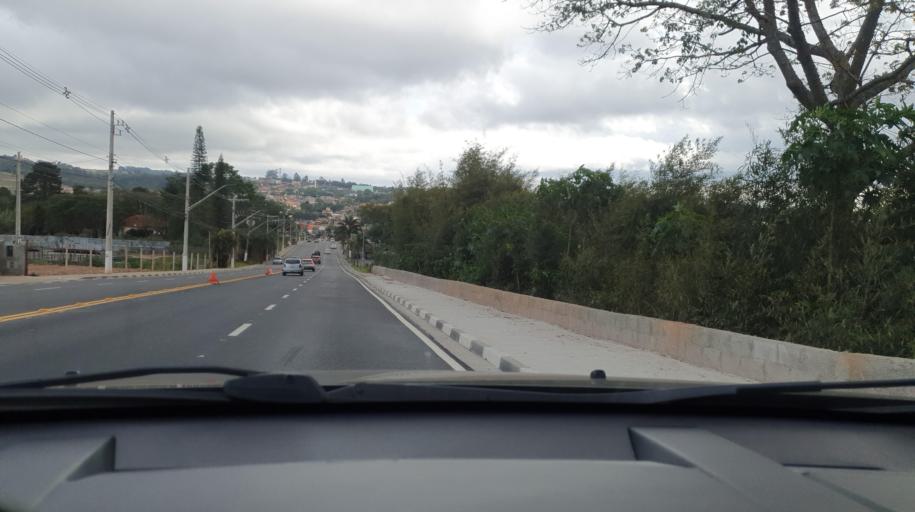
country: BR
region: Sao Paulo
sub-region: Vargem Grande Paulista
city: Vargem Grande Paulista
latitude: -23.6796
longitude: -47.0160
